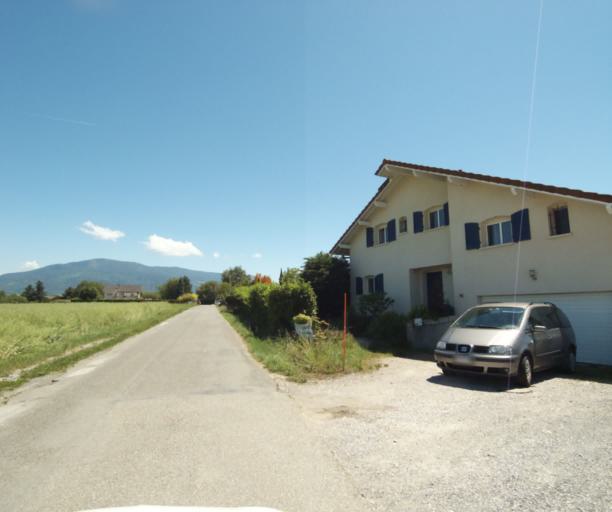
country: FR
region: Rhone-Alpes
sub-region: Departement de la Haute-Savoie
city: Veigy-Foncenex
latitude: 46.2618
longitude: 6.2580
